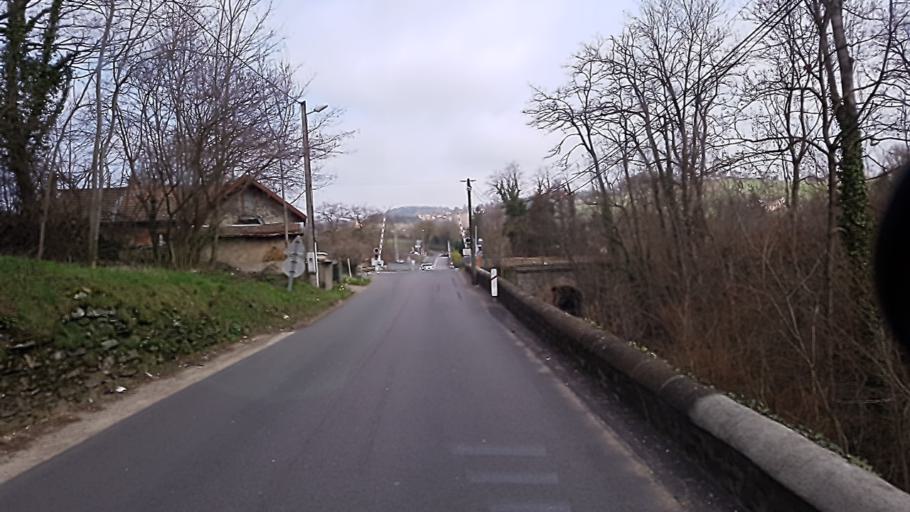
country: FR
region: Rhone-Alpes
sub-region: Departement du Rhone
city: Lozanne
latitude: 45.8548
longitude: 4.6697
